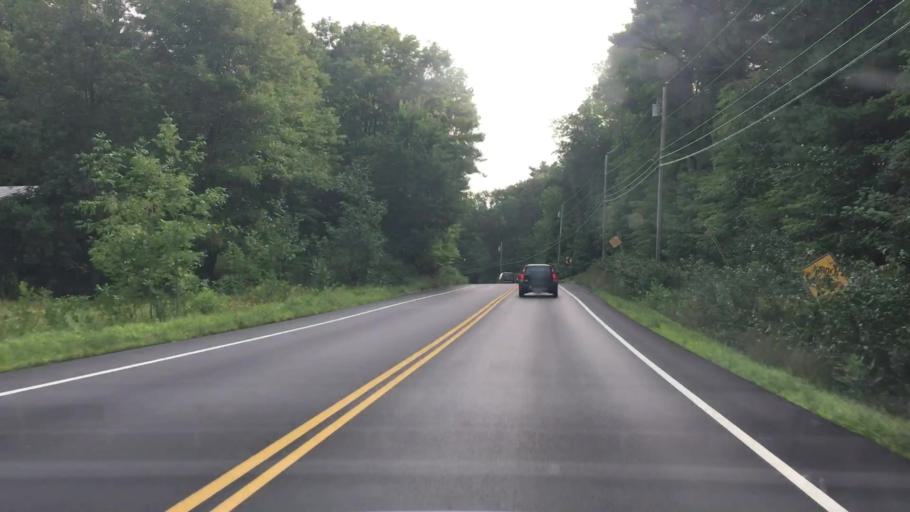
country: US
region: Maine
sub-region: Kennebec County
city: Chelsea
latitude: 44.2443
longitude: -69.7270
